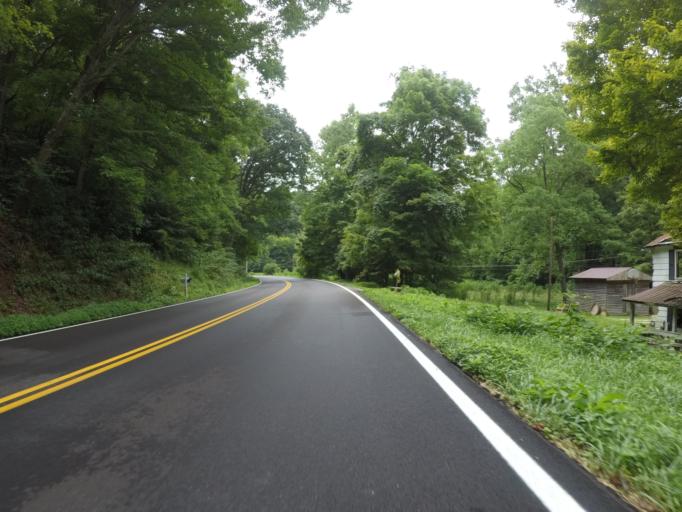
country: US
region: Kentucky
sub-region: Boyd County
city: Catlettsburg
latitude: 38.4236
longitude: -82.6271
